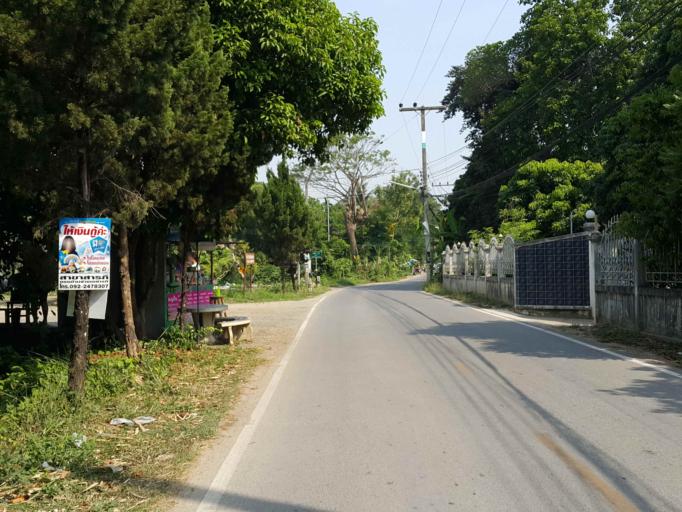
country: TH
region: Chiang Mai
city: Saraphi
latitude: 18.7445
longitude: 99.0523
